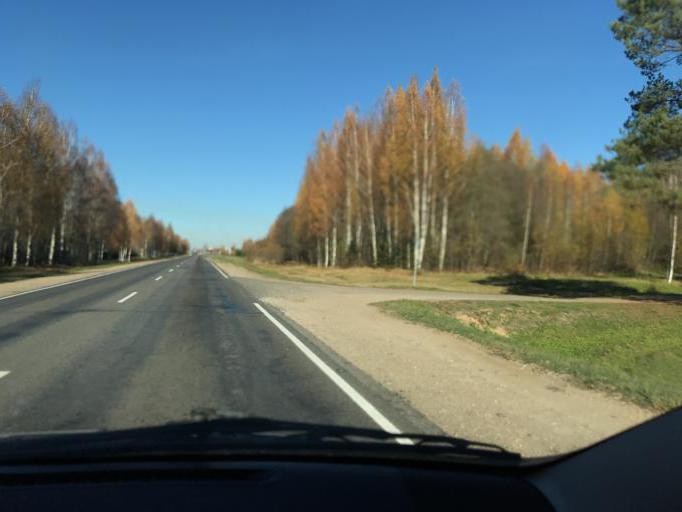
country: BY
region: Vitebsk
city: Polatsk
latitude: 55.4459
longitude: 28.7726
